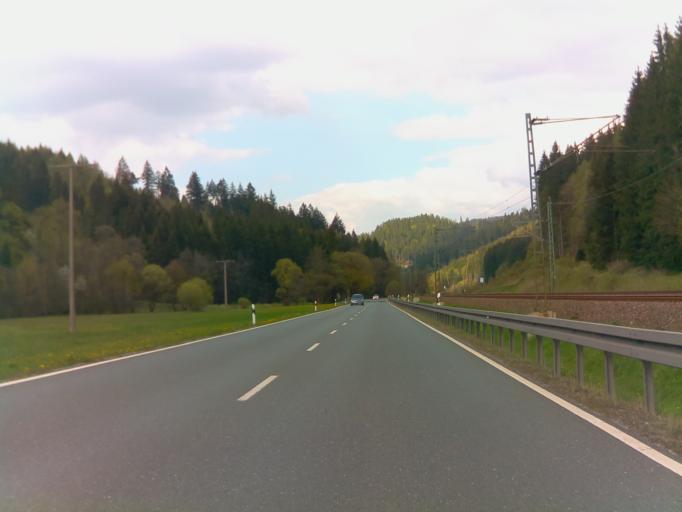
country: DE
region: Bavaria
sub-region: Upper Franconia
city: Pressig
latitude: 50.3739
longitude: 11.3320
